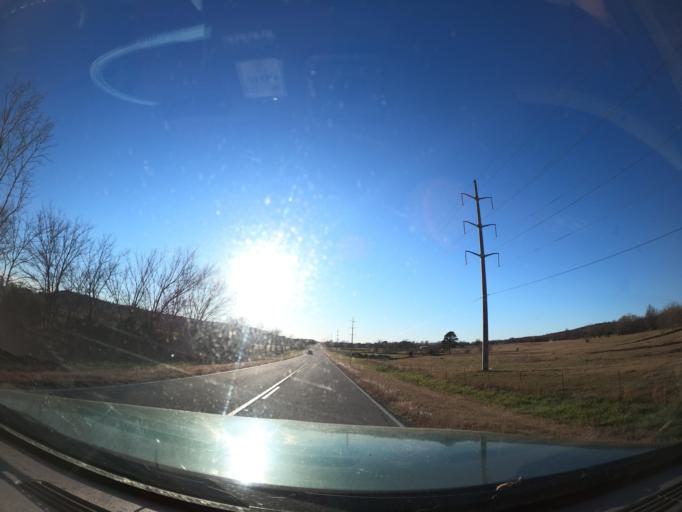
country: US
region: Oklahoma
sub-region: Pittsburg County
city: Hartshorne
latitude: 34.8862
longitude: -95.4862
